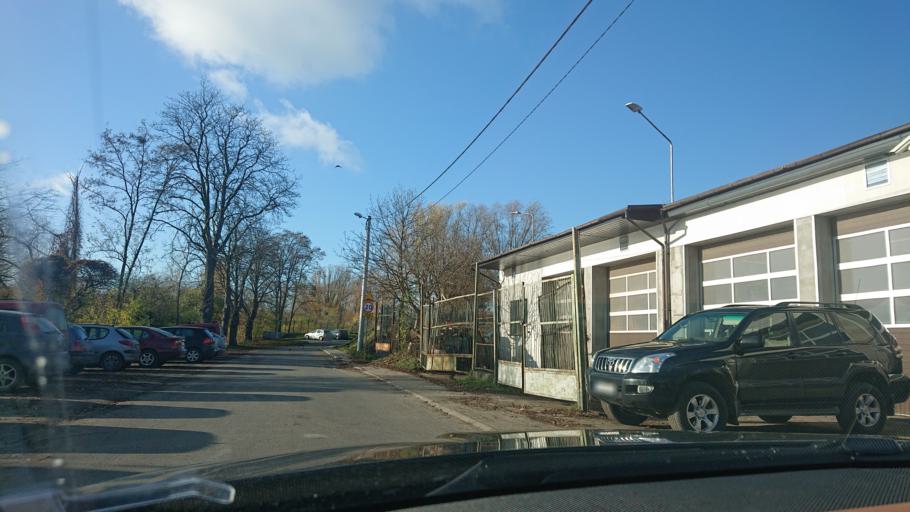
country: PL
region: Greater Poland Voivodeship
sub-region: Powiat gnieznienski
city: Gniezno
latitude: 52.5456
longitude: 17.5954
